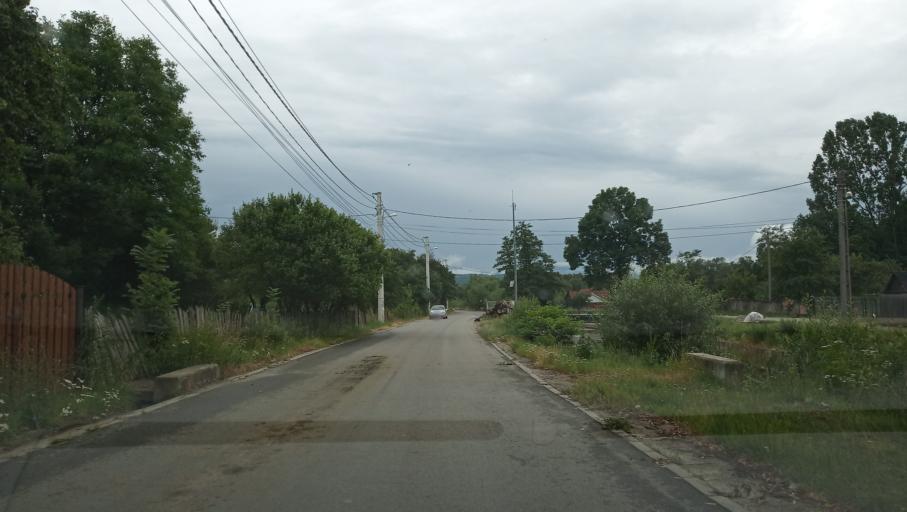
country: RO
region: Hunedoara
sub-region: Oras Petrila
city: Petrila
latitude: 45.4593
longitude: 23.4192
